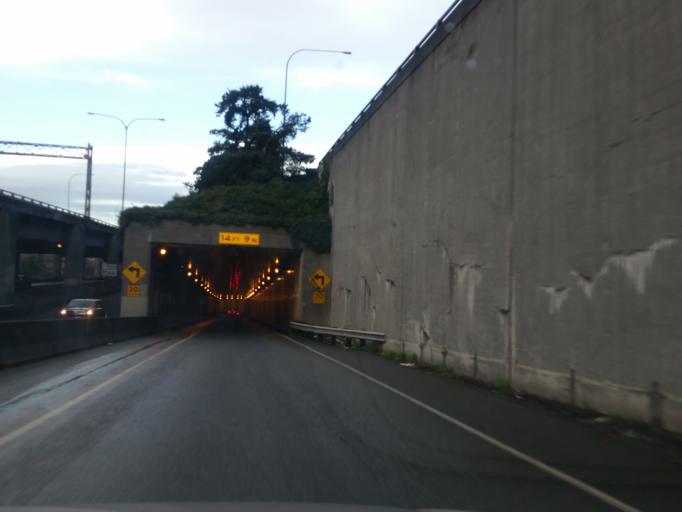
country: US
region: Washington
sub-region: King County
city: Seattle
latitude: 47.6227
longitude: -122.3283
